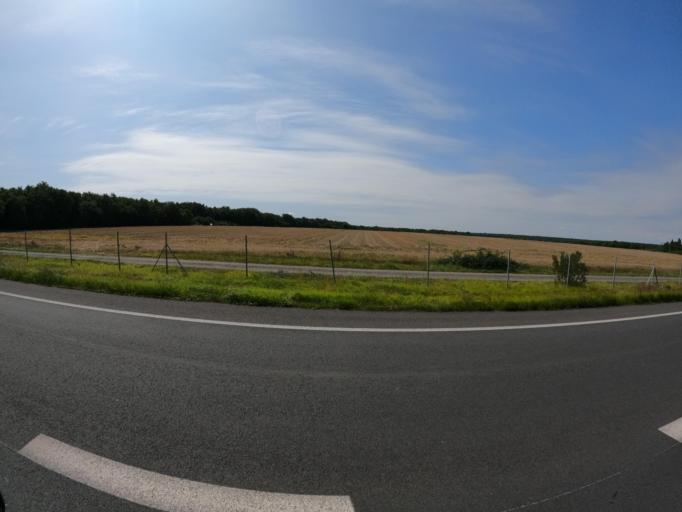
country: FR
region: Poitou-Charentes
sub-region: Departement des Deux-Sevres
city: Saint-Hilaire-la-Palud
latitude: 46.2110
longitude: -0.7461
